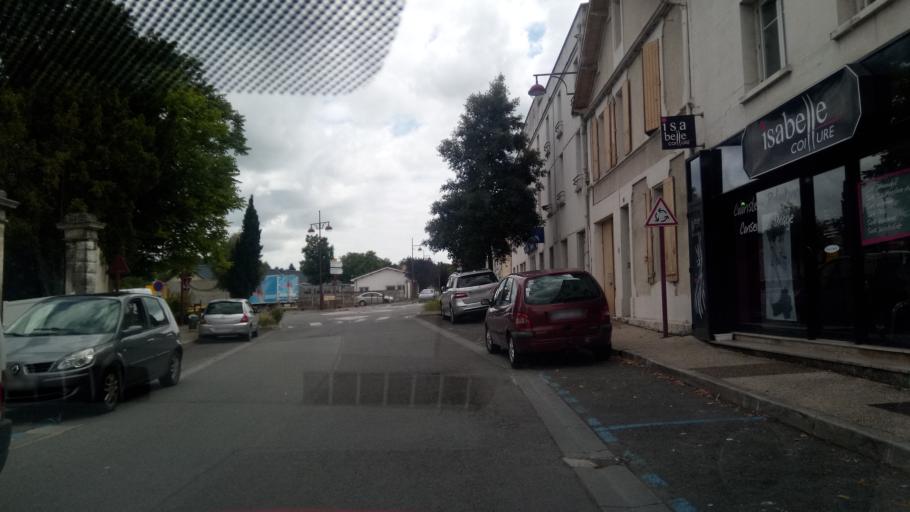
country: FR
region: Poitou-Charentes
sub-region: Departement de la Charente
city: La Couronne
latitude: 45.6055
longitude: 0.1000
